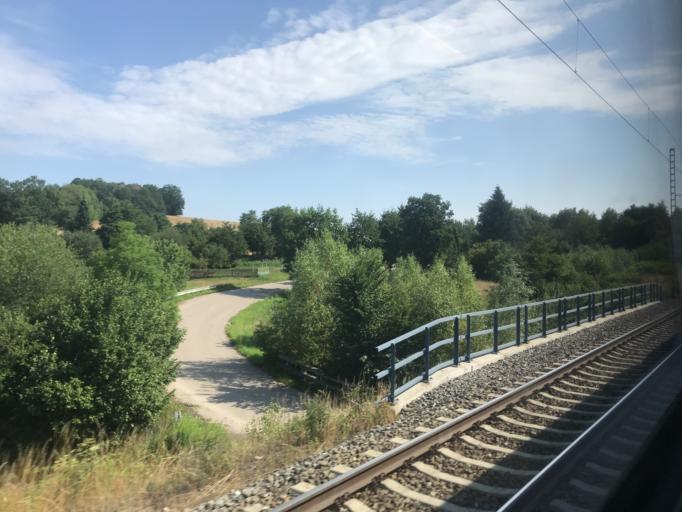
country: CZ
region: Central Bohemia
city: Bystrice
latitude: 49.6976
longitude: 14.6497
